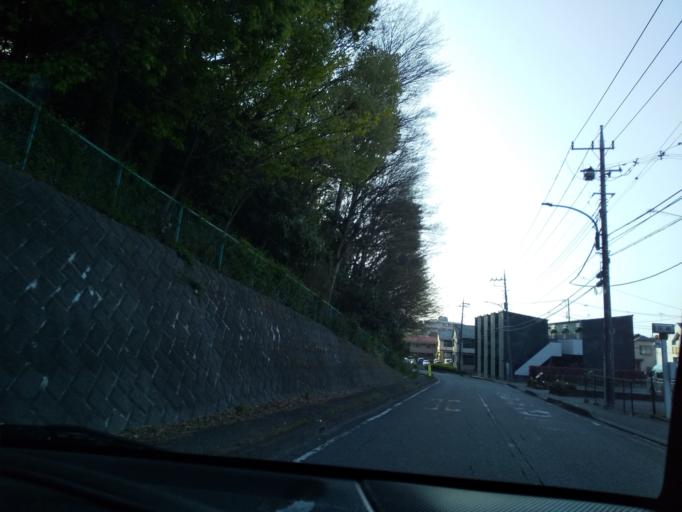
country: JP
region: Kanagawa
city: Zama
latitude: 35.5571
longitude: 139.3644
